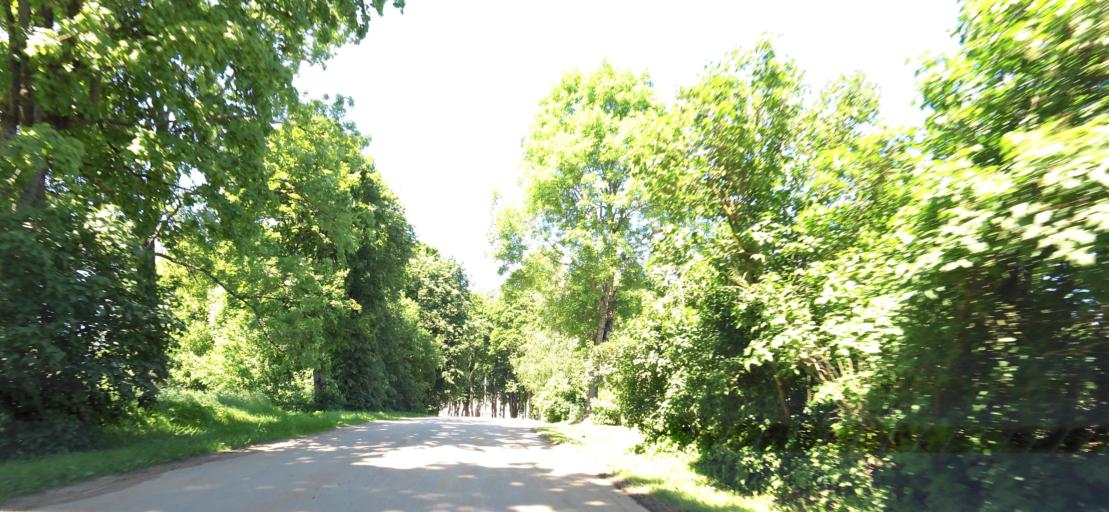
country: LT
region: Vilnius County
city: Pasilaiciai
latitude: 54.9845
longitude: 25.2252
